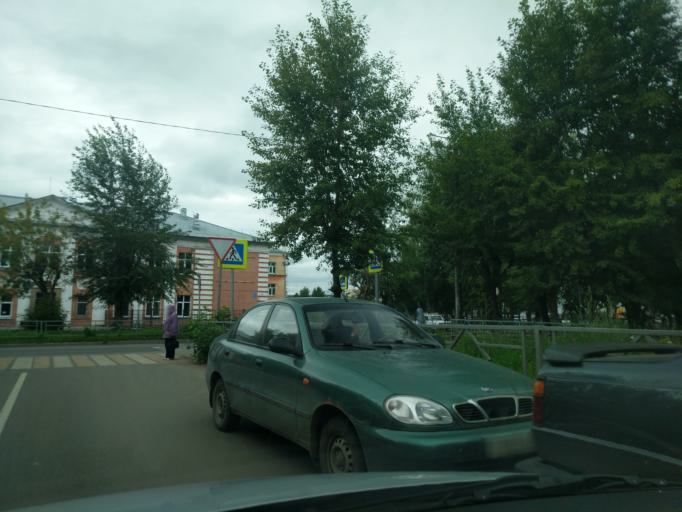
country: RU
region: Kirov
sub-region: Kirovo-Chepetskiy Rayon
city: Kirov
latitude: 58.6356
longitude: 49.6155
